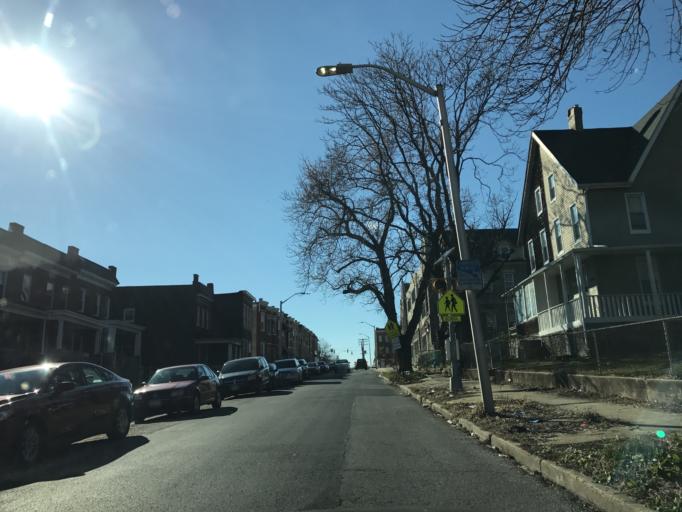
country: US
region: Maryland
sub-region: Baltimore County
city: Charlestown
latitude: 39.2981
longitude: -76.6633
